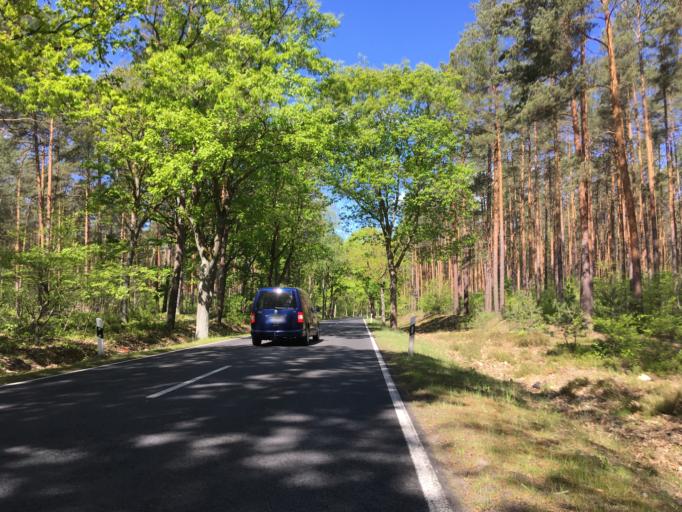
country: DE
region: Brandenburg
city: Birkenwerder
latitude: 52.7196
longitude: 13.3356
